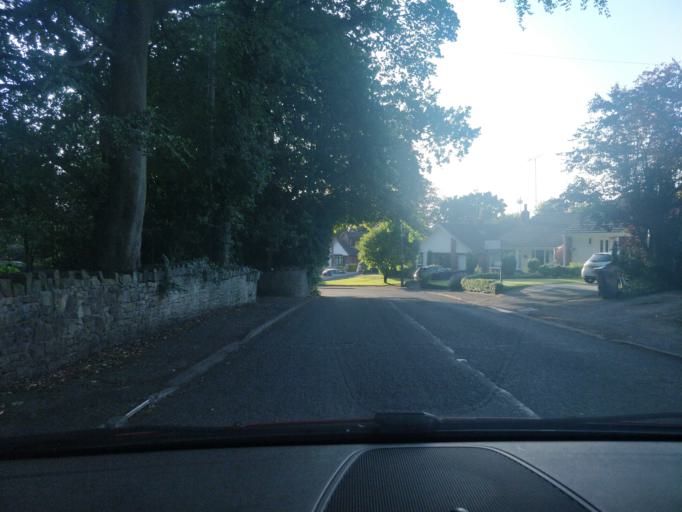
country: GB
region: England
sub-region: Lancashire
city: Parbold
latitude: 53.6025
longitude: -2.7661
